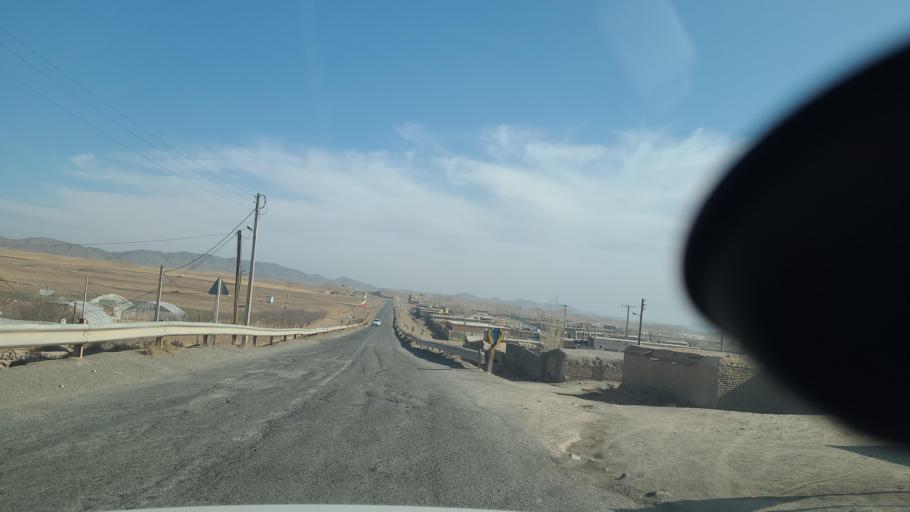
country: IR
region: Razavi Khorasan
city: Fariman
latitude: 35.5928
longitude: 59.6794
